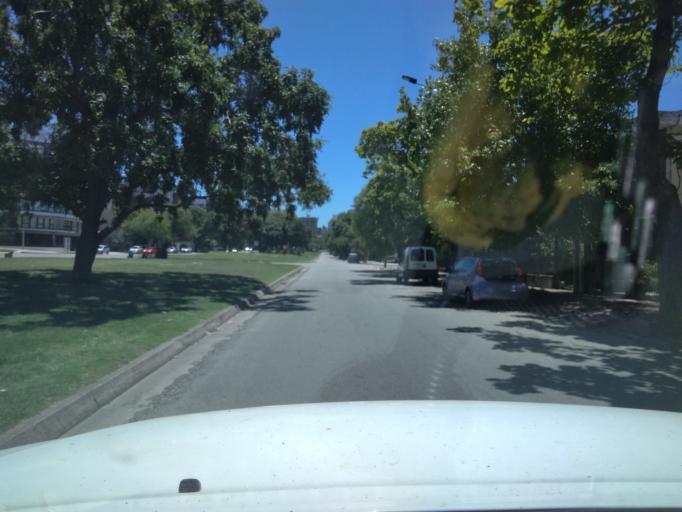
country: UY
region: Canelones
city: Paso de Carrasco
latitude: -34.8930
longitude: -56.1063
